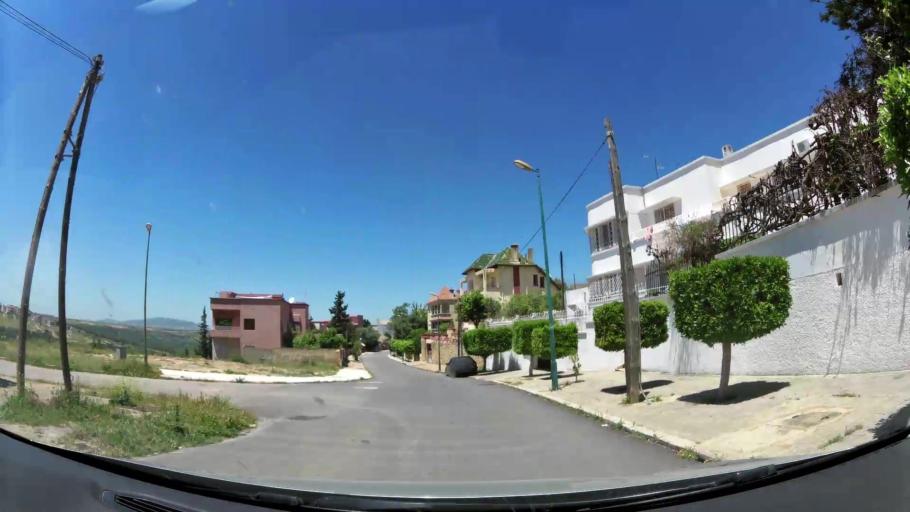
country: MA
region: Meknes-Tafilalet
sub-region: Meknes
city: Meknes
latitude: 33.9093
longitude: -5.5623
